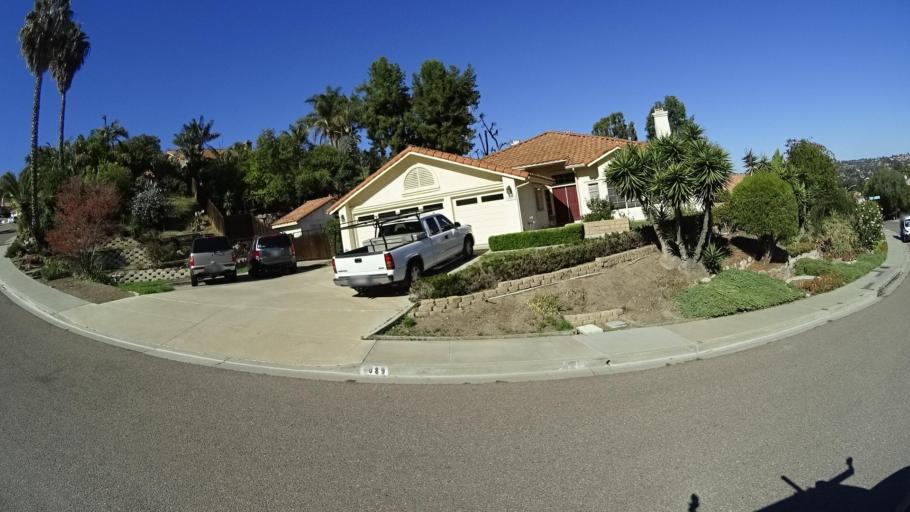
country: US
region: California
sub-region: San Diego County
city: Bonita
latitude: 32.6628
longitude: -117.0143
